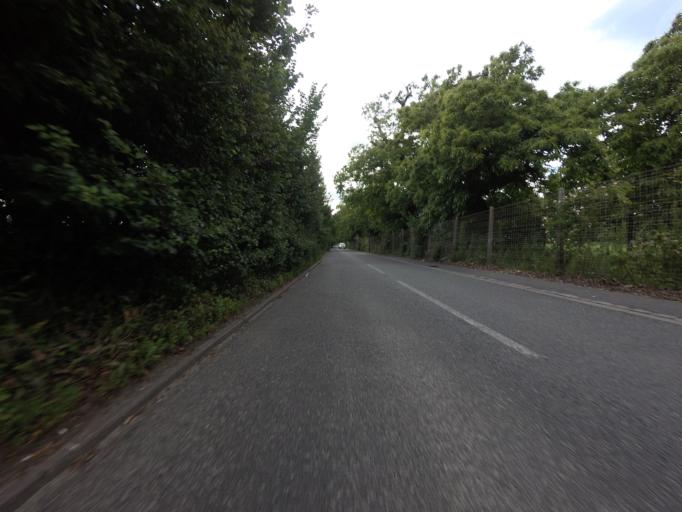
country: GB
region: England
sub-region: Greater London
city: Sidcup
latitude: 51.4224
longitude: 0.1198
